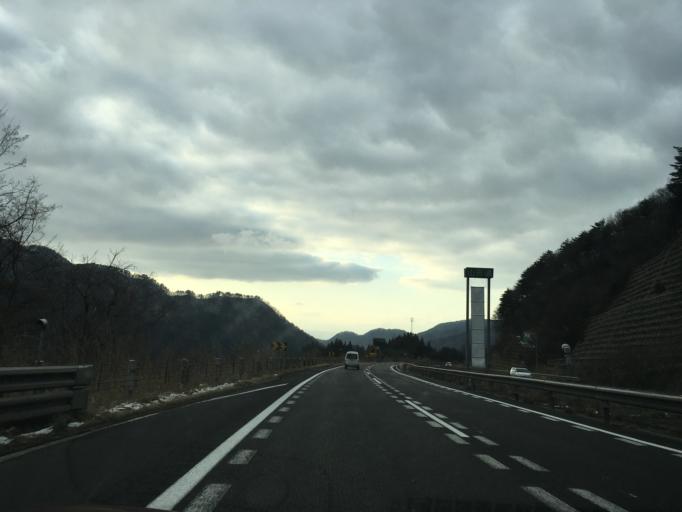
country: JP
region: Yamagata
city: Yamagata-shi
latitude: 38.2270
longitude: 140.4128
